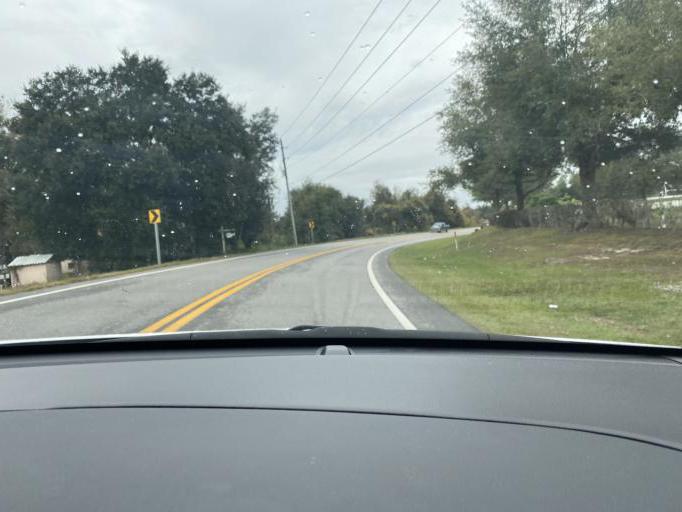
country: US
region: Florida
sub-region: Lake County
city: Mascotte
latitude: 28.5806
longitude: -81.8706
